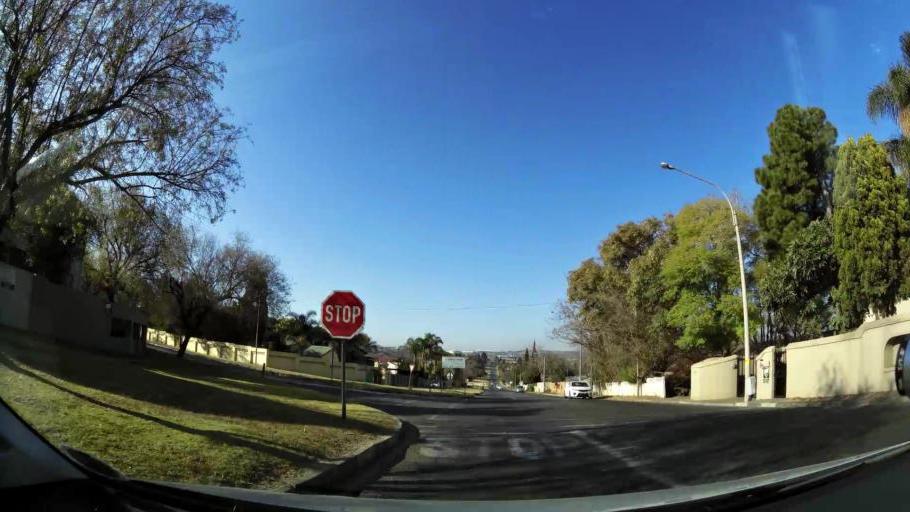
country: ZA
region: Gauteng
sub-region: City of Johannesburg Metropolitan Municipality
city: Modderfontein
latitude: -26.1298
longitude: 28.1643
